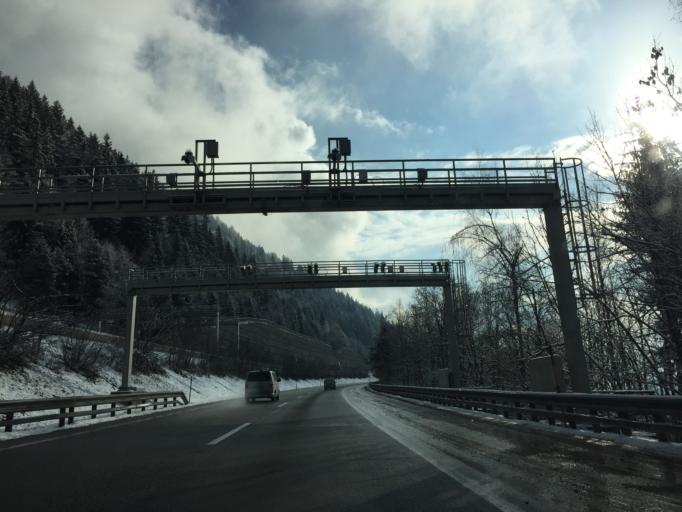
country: AT
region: Salzburg
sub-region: Politischer Bezirk Sankt Johann im Pongau
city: Huttau
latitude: 47.4338
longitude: 13.2709
